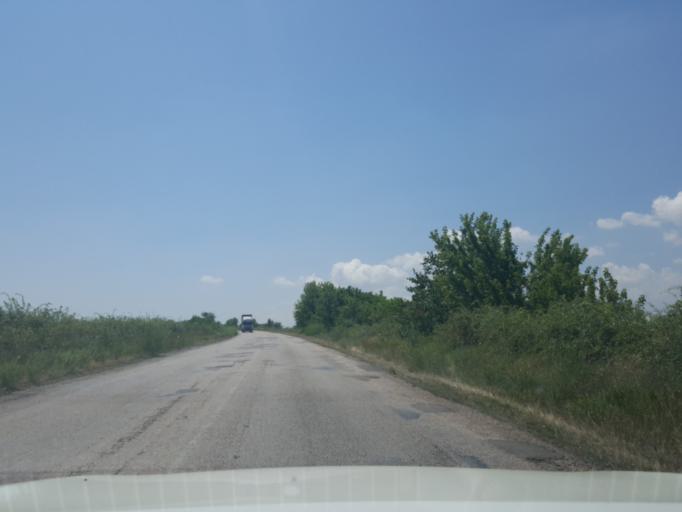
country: UA
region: Odessa
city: Starokozache
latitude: 46.3940
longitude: 30.0926
